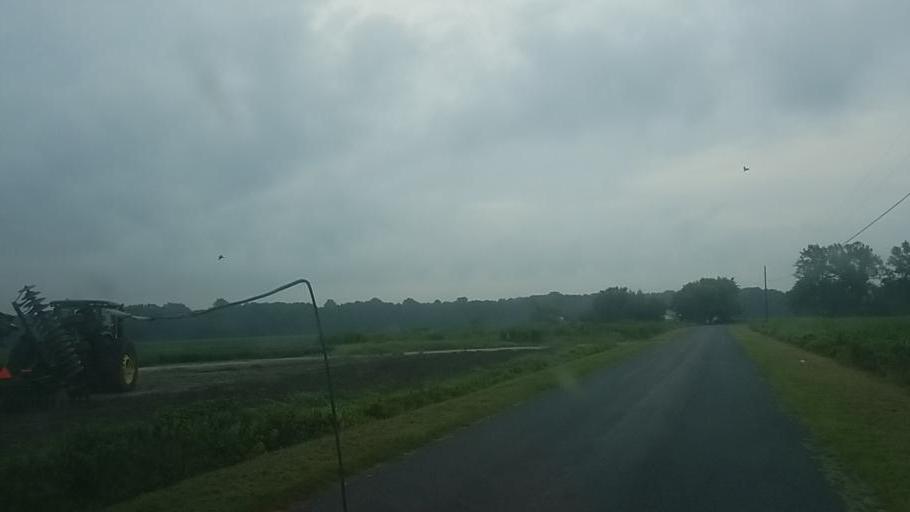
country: US
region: Maryland
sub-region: Wicomico County
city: Pittsville
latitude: 38.4490
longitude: -75.3507
